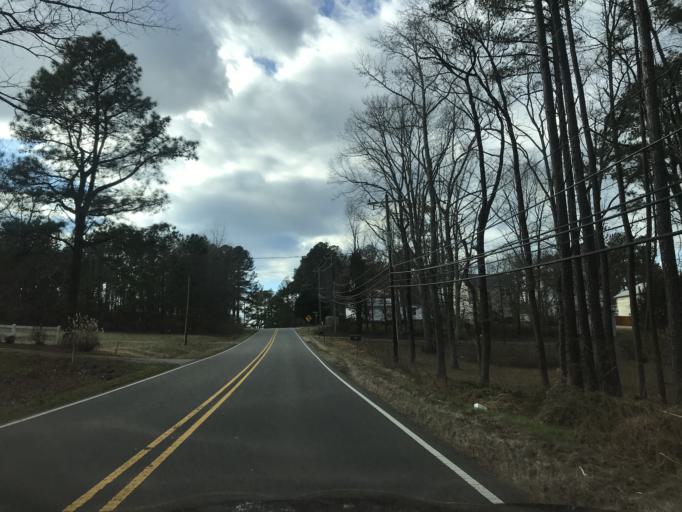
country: US
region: North Carolina
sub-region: Durham County
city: Durham
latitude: 35.9682
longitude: -78.8370
